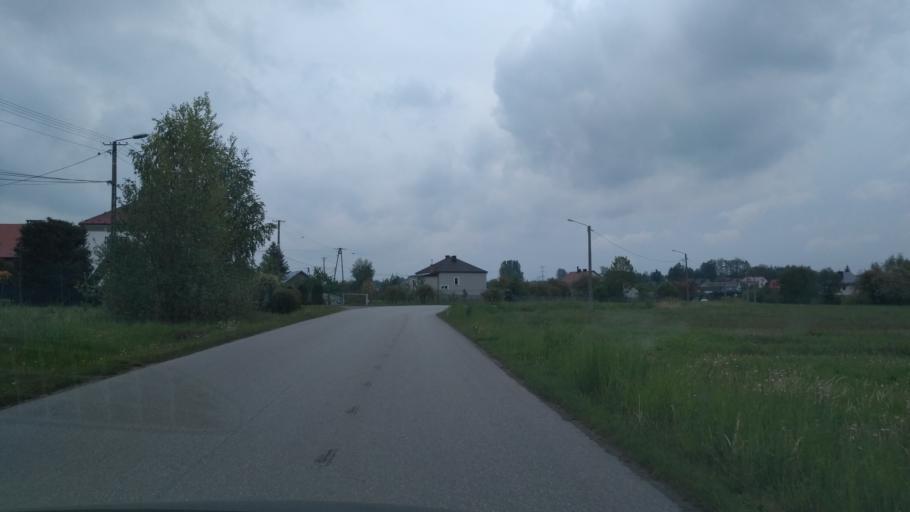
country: PL
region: Subcarpathian Voivodeship
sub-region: Powiat kolbuszowski
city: Kolbuszowa
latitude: 50.1974
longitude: 21.8095
